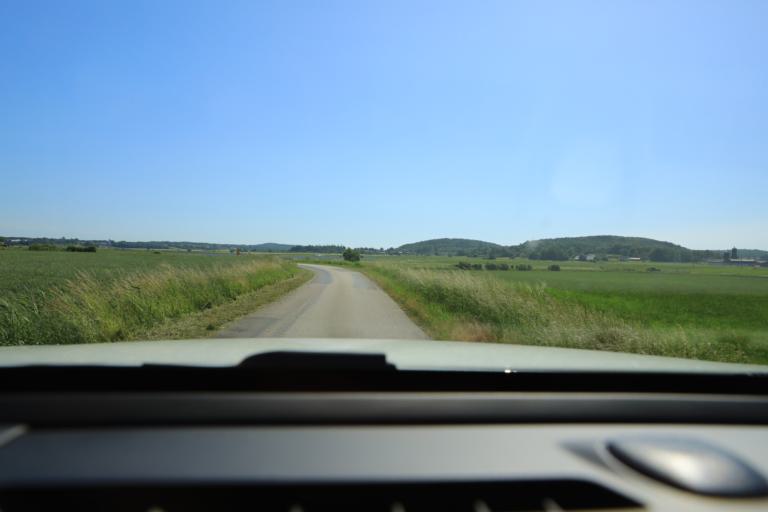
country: SE
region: Halland
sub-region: Varbergs Kommun
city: Veddige
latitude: 57.1857
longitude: 12.3138
